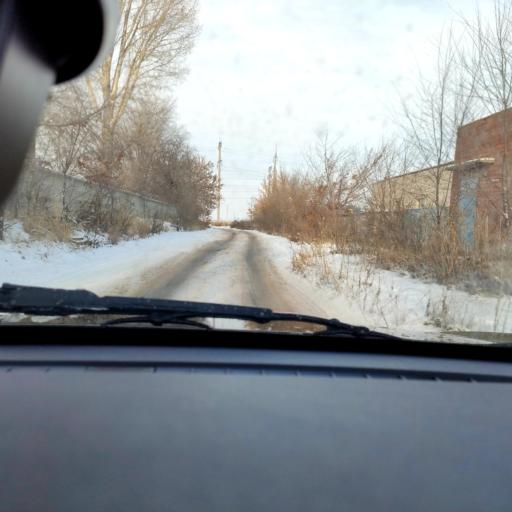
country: RU
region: Samara
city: Tol'yatti
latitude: 53.5421
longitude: 49.4189
